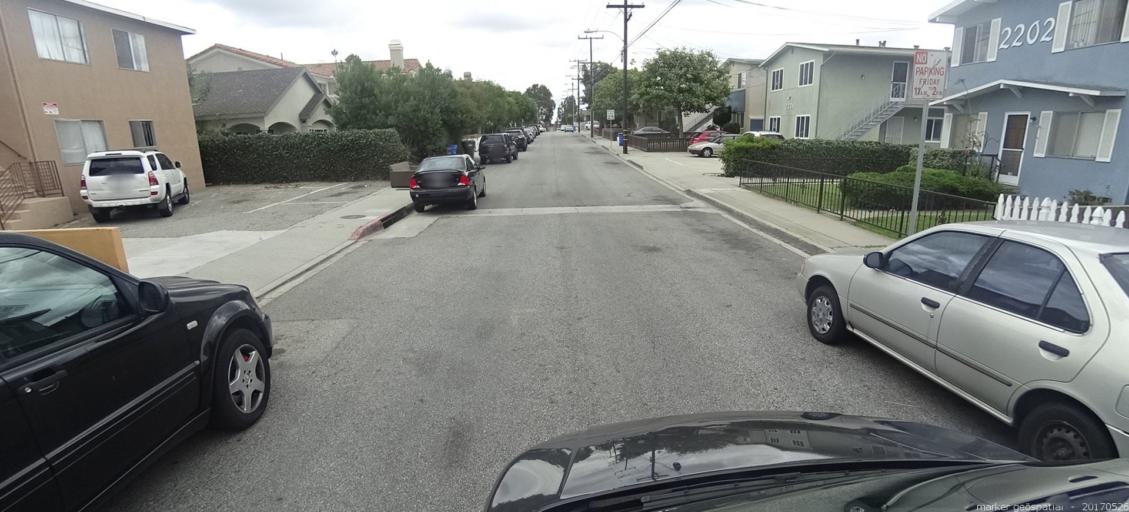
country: US
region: California
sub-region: Los Angeles County
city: Lawndale
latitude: 33.8738
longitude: -118.3726
